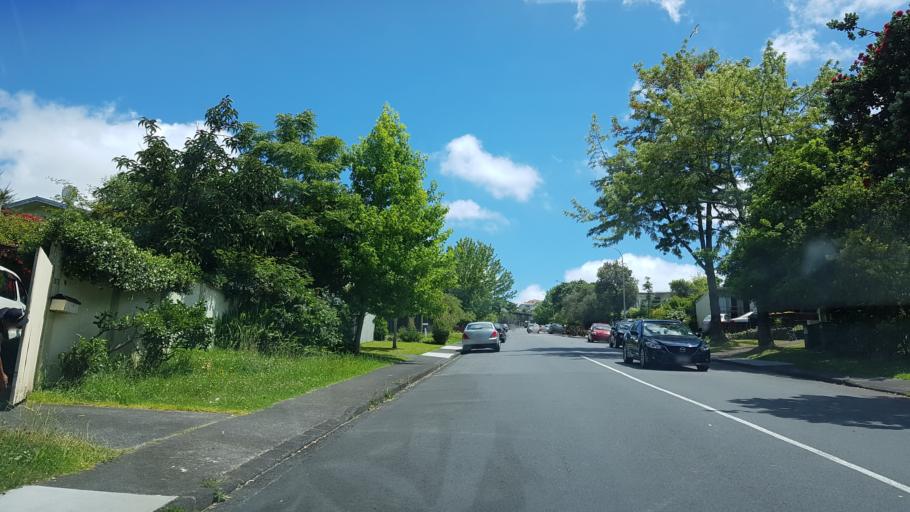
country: NZ
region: Auckland
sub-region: Auckland
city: North Shore
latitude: -36.7783
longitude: 174.7151
